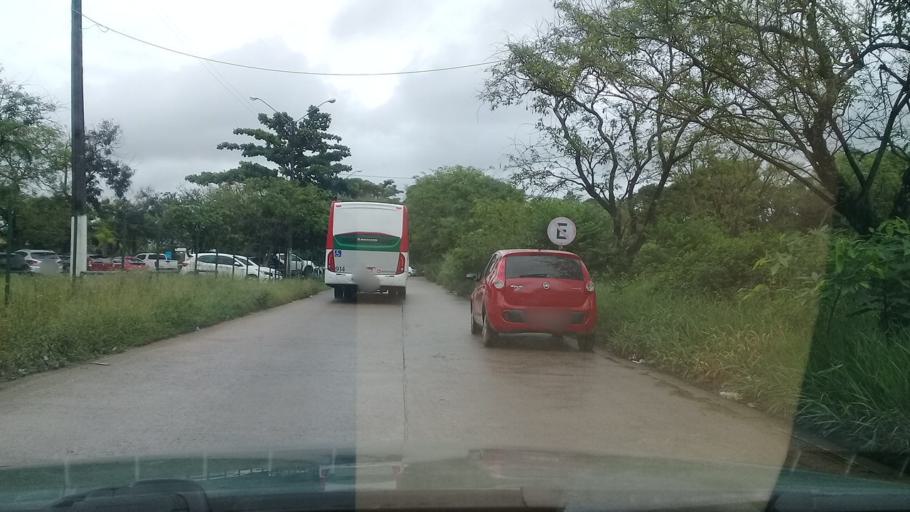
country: BR
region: Pernambuco
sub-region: Jaboatao Dos Guararapes
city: Jaboatao dos Guararapes
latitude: -8.0629
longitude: -34.9822
